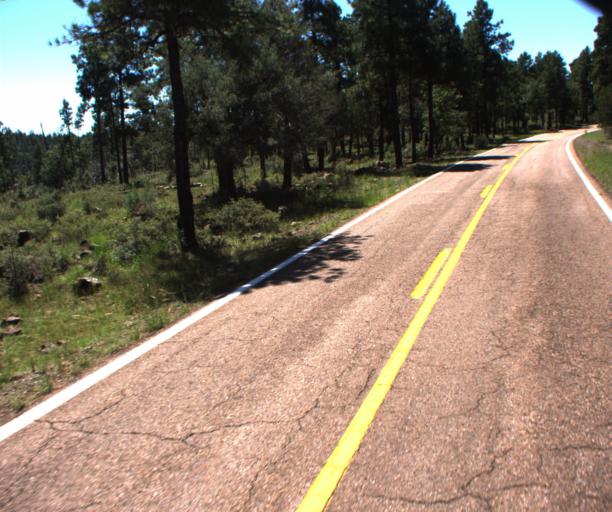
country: US
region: Arizona
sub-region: Greenlee County
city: Morenci
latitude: 33.5075
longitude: -109.3227
